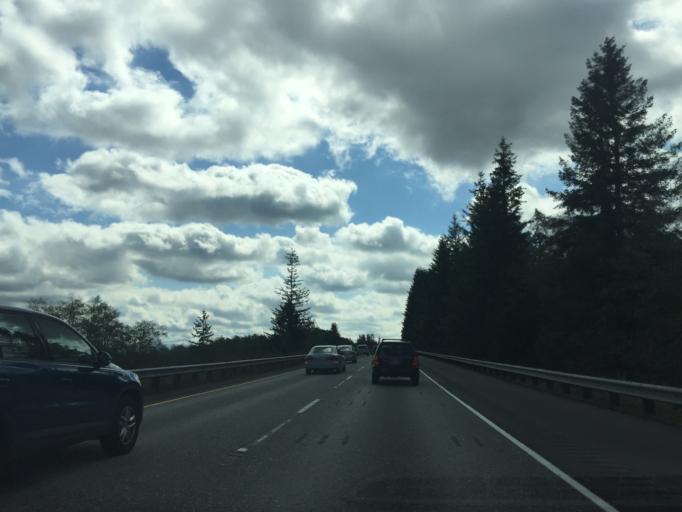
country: US
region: Washington
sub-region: Whatcom County
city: Sudden Valley
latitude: 48.6348
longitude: -122.3605
